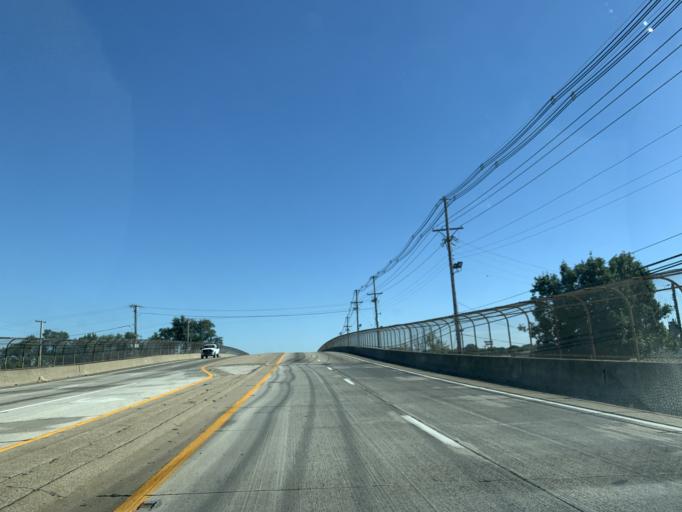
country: US
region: Kentucky
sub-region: Jefferson County
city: Audubon Park
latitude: 38.1924
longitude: -85.7060
